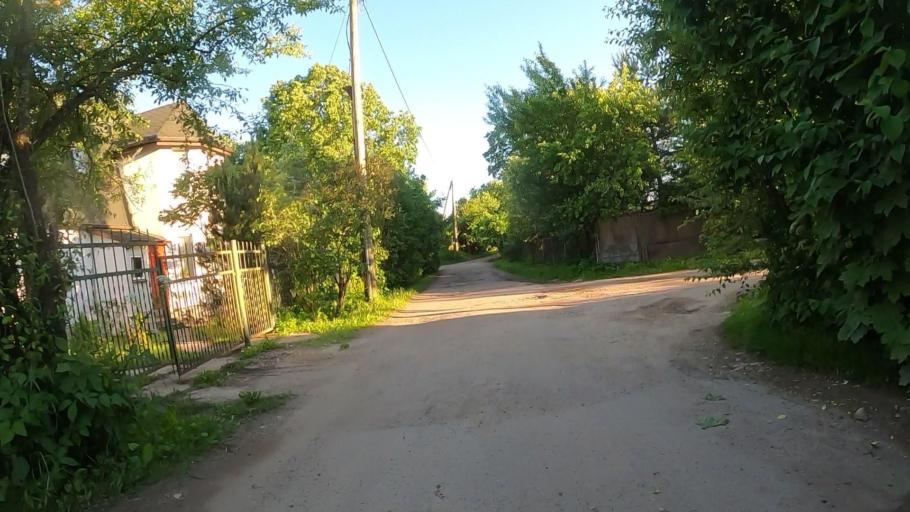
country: LV
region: Kekava
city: Kekava
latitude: 56.8631
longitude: 24.2632
